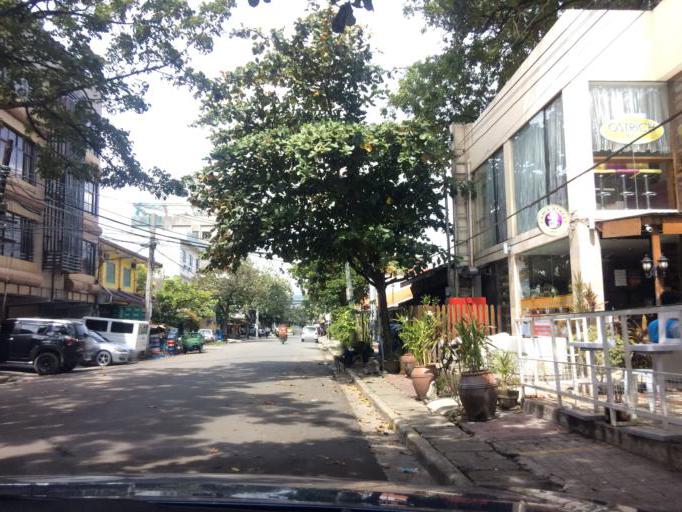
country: PH
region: Central Visayas
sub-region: Province of Cebu
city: Cebu City
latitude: 10.3155
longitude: 123.8933
